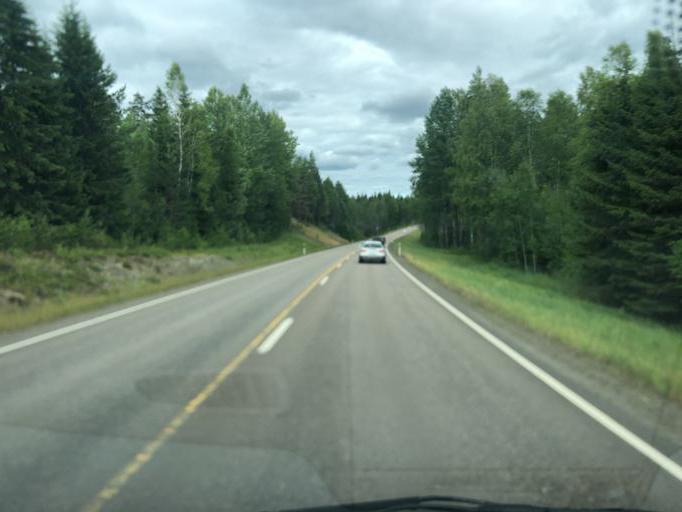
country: FI
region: Kymenlaakso
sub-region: Kouvola
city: Kouvola
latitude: 61.0394
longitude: 26.9923
